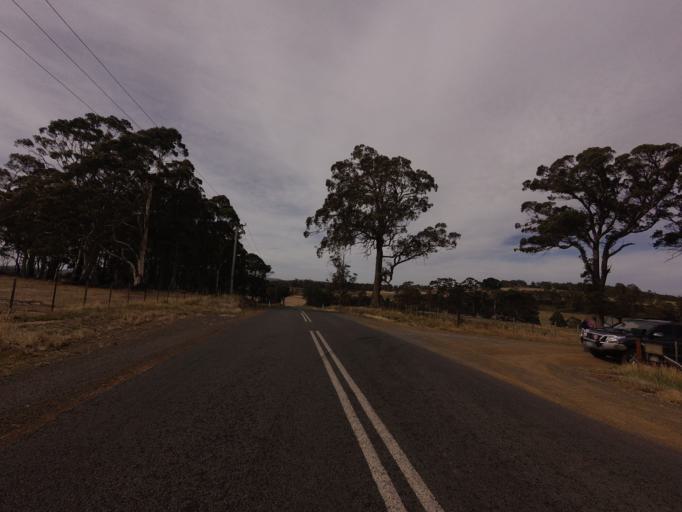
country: AU
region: Tasmania
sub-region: Sorell
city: Sorell
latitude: -42.4088
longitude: 147.4549
